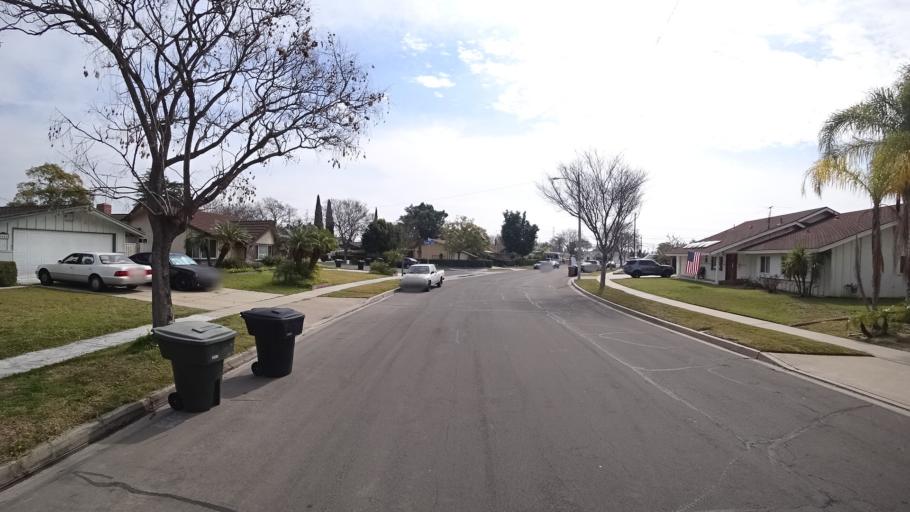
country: US
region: California
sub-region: Orange County
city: Garden Grove
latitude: 33.8117
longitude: -117.9472
